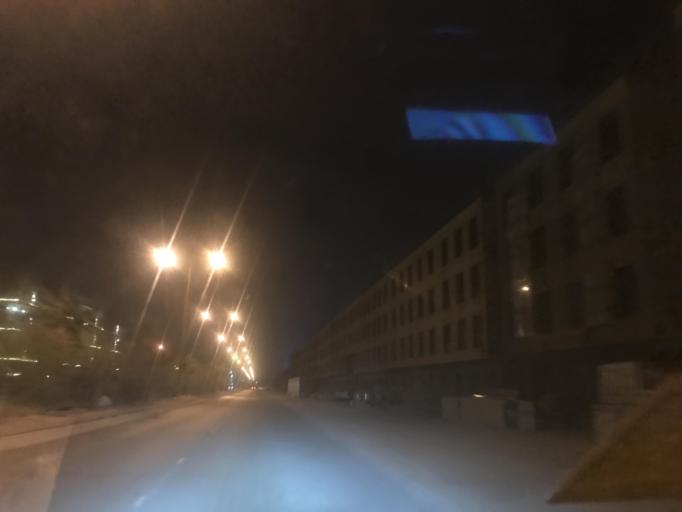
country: SA
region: Ar Riyad
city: Riyadh
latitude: 24.8051
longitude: 46.5911
